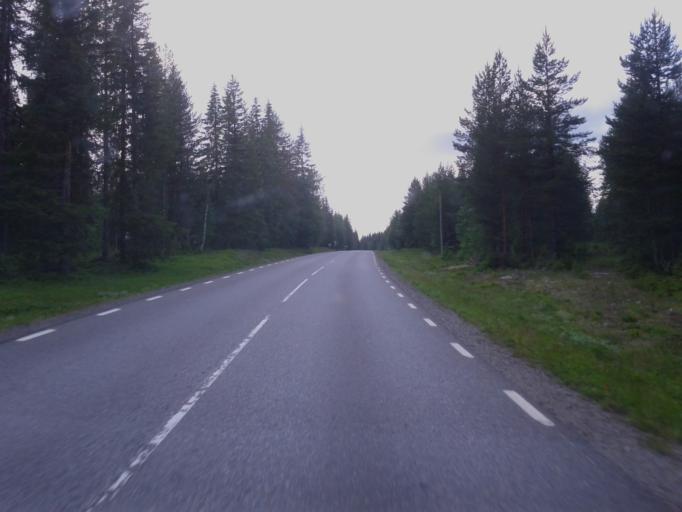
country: SE
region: Vaesterbotten
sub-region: Mala Kommun
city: Mala
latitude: 65.2289
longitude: 18.4723
